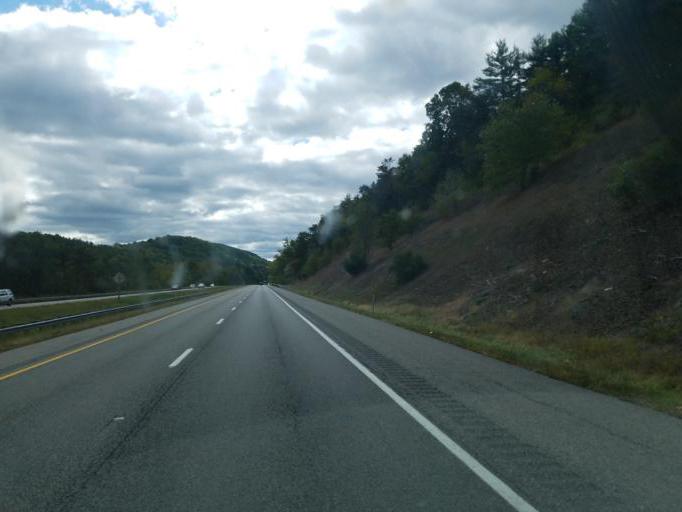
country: US
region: Maryland
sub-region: Washington County
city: Hancock
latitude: 39.7106
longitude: -78.2334
